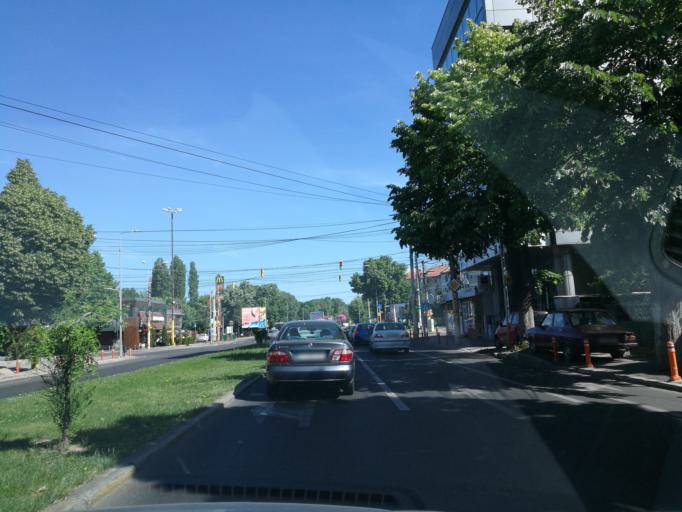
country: RO
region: Constanta
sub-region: Municipiul Constanta
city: Constanta
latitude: 44.2043
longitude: 28.6447
